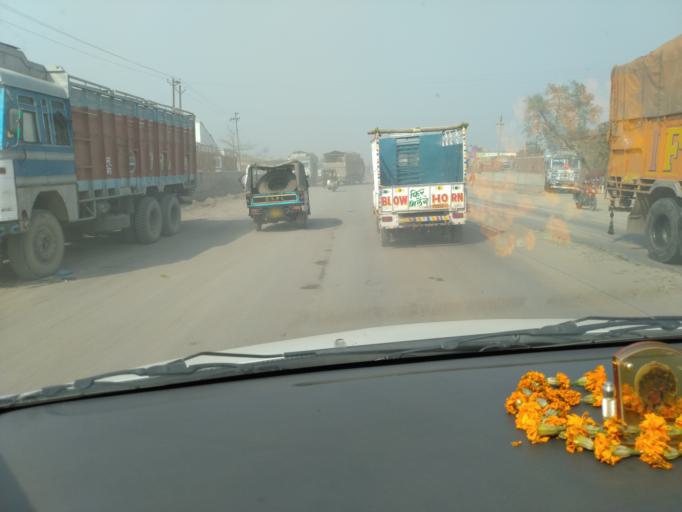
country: IN
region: Bihar
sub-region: Rohtas
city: Dehri
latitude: 24.9153
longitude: 84.1583
